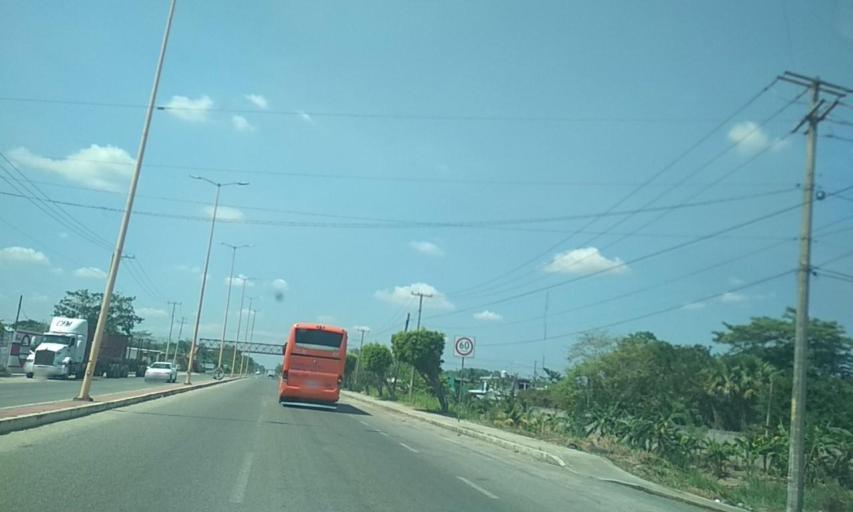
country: MX
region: Tabasco
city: Huimanguillo
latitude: 17.8399
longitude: -93.3977
